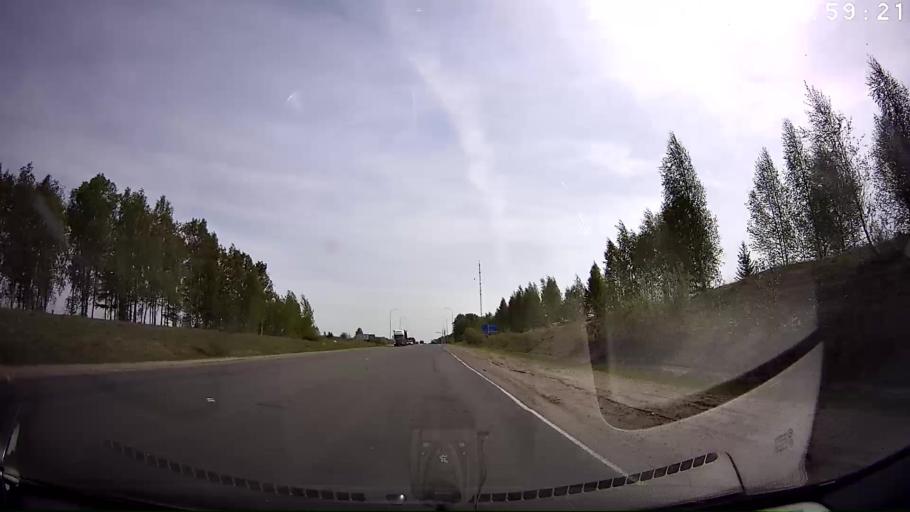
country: RU
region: Mariy-El
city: Sovetskiy
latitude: 56.7530
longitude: 48.5081
